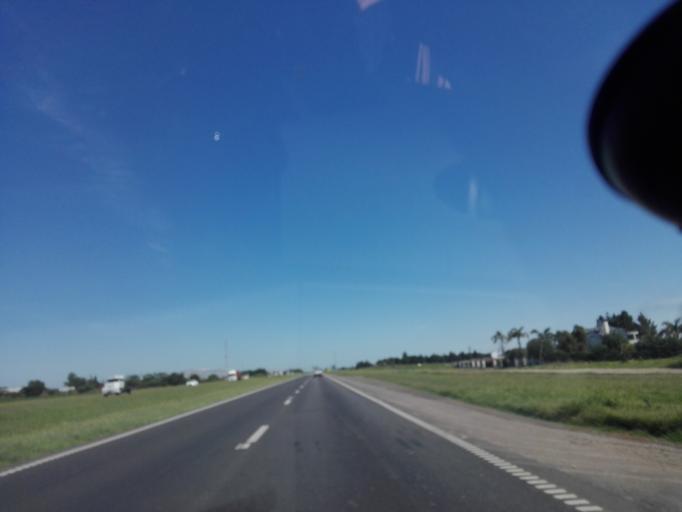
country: AR
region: Buenos Aires
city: San Nicolas de los Arroyos
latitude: -33.3734
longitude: -60.2426
